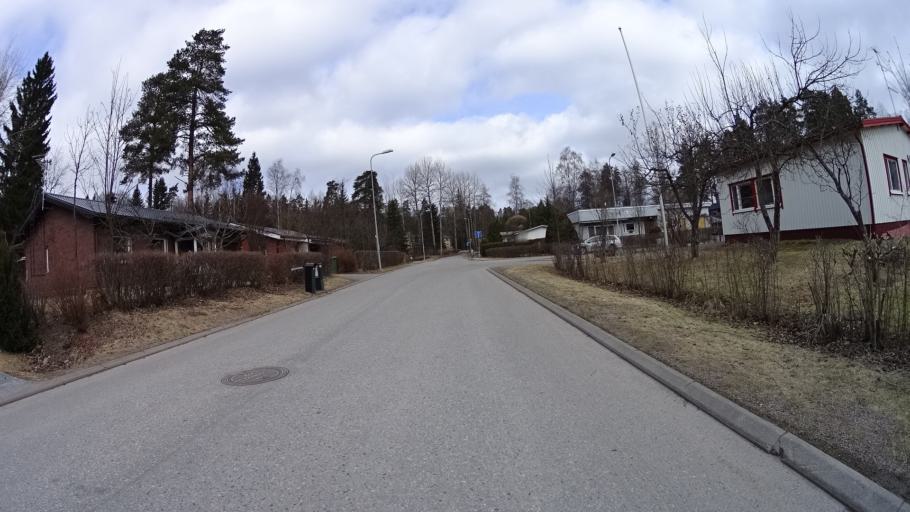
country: FI
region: Uusimaa
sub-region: Helsinki
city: Kilo
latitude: 60.2518
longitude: 24.8067
